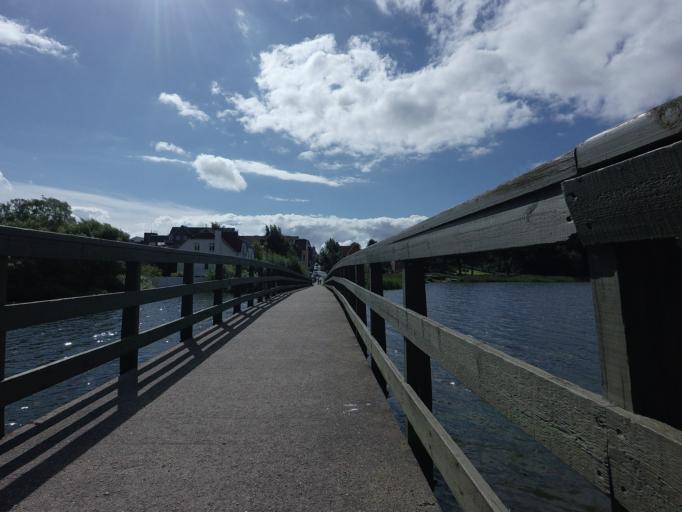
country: DK
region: Central Jutland
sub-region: Silkeborg Kommune
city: Silkeborg
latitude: 56.1705
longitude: 9.5423
